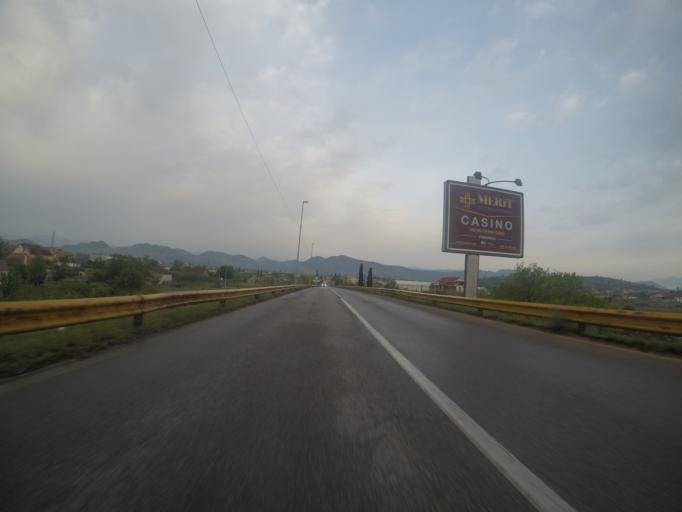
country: ME
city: Mojanovici
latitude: 42.3658
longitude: 19.2341
